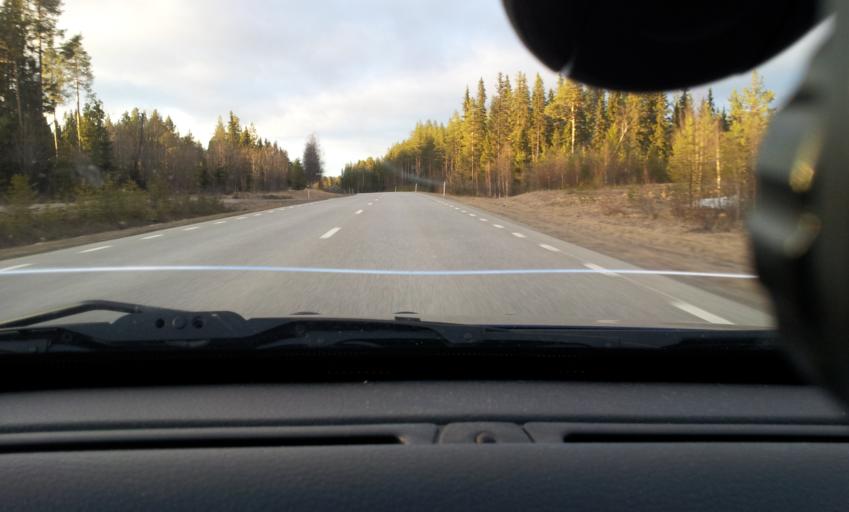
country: SE
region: Jaemtland
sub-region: Bergs Kommun
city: Hoverberg
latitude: 62.7146
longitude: 14.4140
